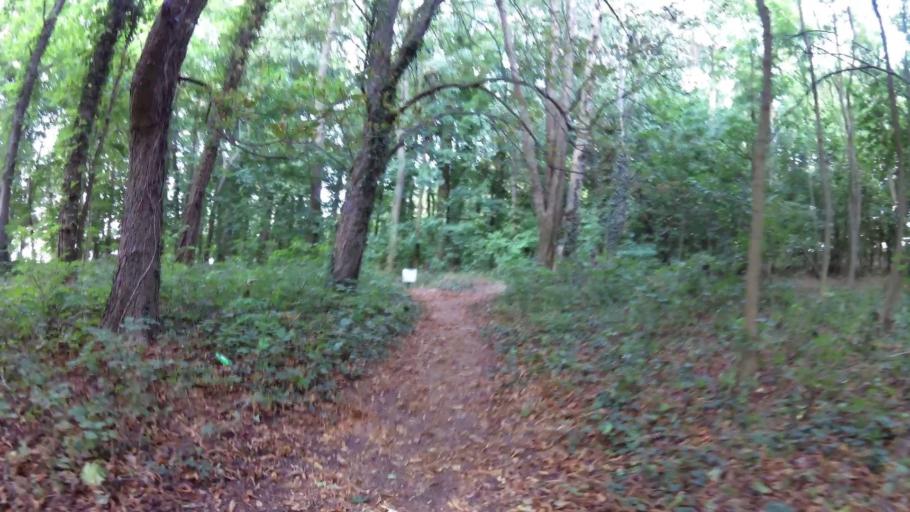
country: PL
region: West Pomeranian Voivodeship
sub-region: Powiat gryfinski
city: Moryn
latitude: 52.8604
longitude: 14.4229
